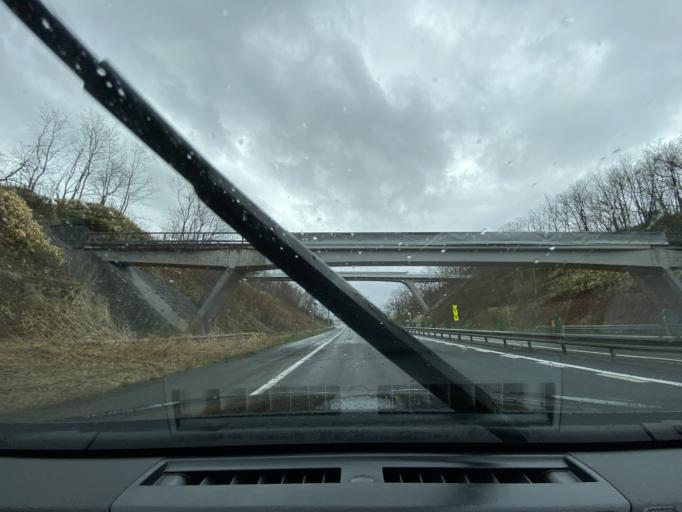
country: JP
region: Hokkaido
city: Bibai
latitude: 43.2489
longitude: 141.8308
